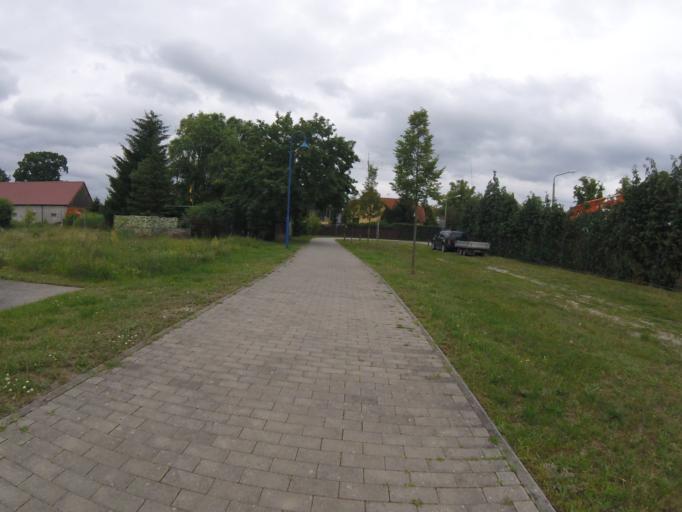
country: DE
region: Brandenburg
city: Bestensee
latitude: 52.2443
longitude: 13.6265
